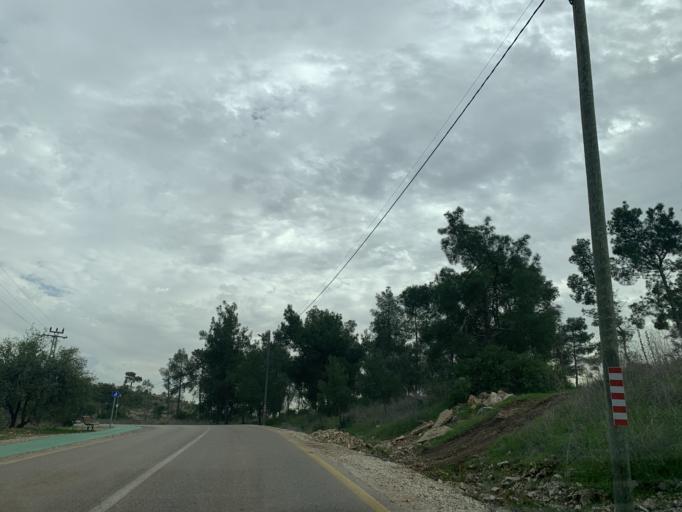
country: IL
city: Nirit
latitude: 32.1440
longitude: 34.9835
